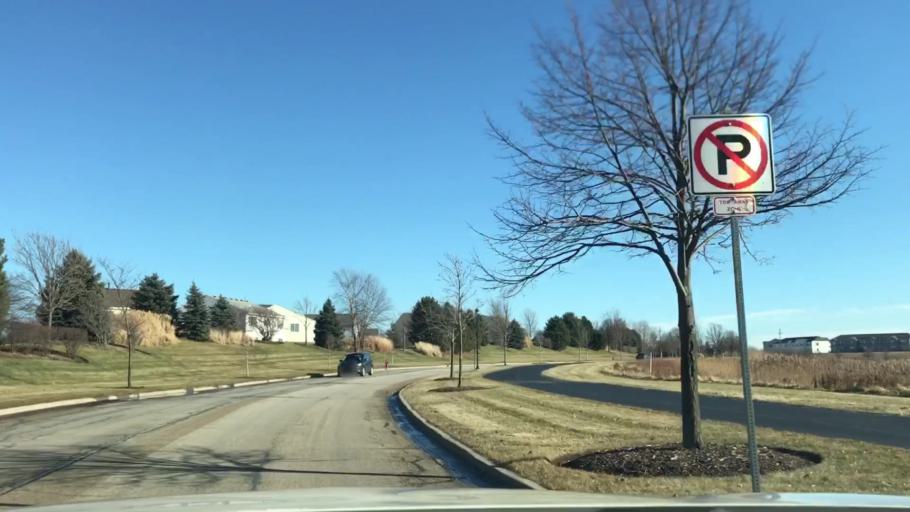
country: US
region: Illinois
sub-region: Kane County
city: Pingree Grove
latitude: 42.0787
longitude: -88.4214
